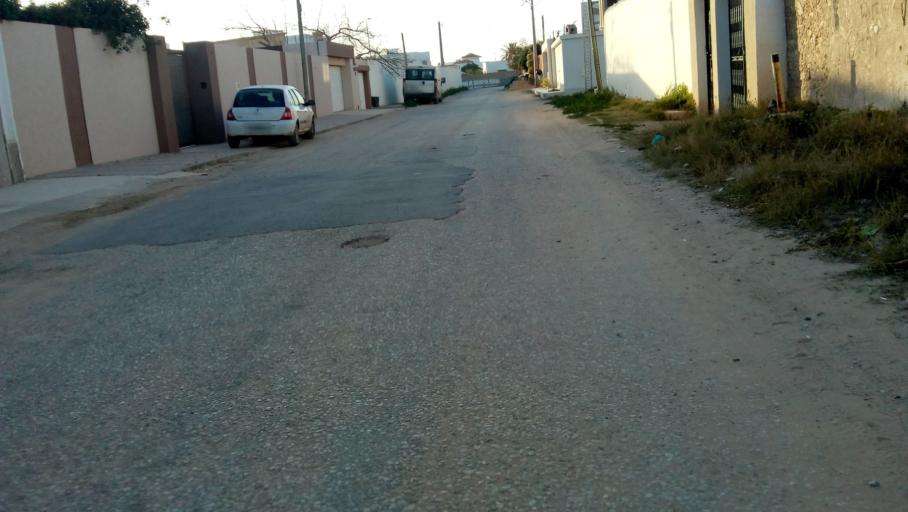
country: TN
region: Safaqis
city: Sfax
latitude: 34.7530
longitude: 10.7331
